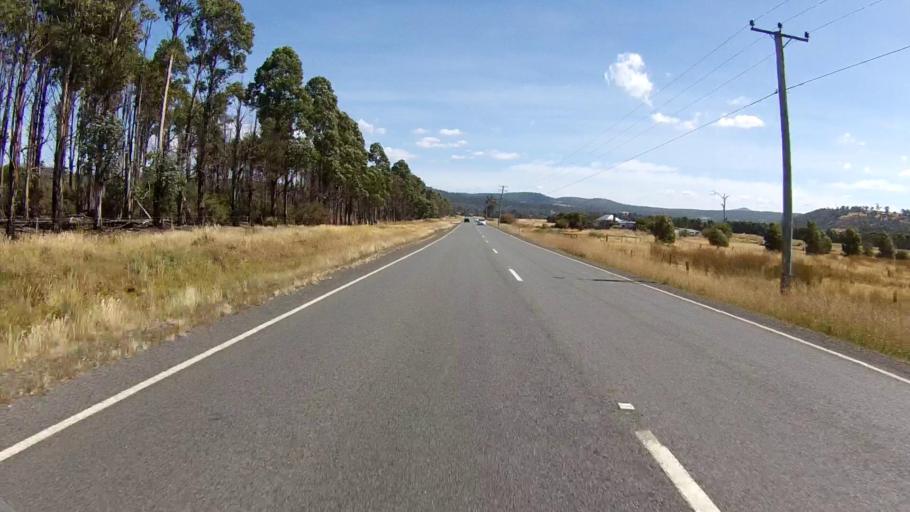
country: AU
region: Tasmania
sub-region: Sorell
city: Sorell
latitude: -42.6052
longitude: 147.7461
